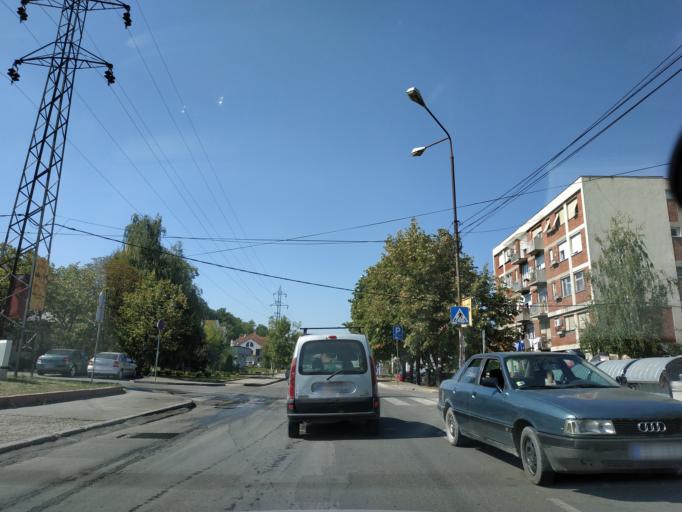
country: RS
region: Central Serbia
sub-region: Sumadijski Okrug
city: Arangelovac
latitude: 44.3015
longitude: 20.5704
